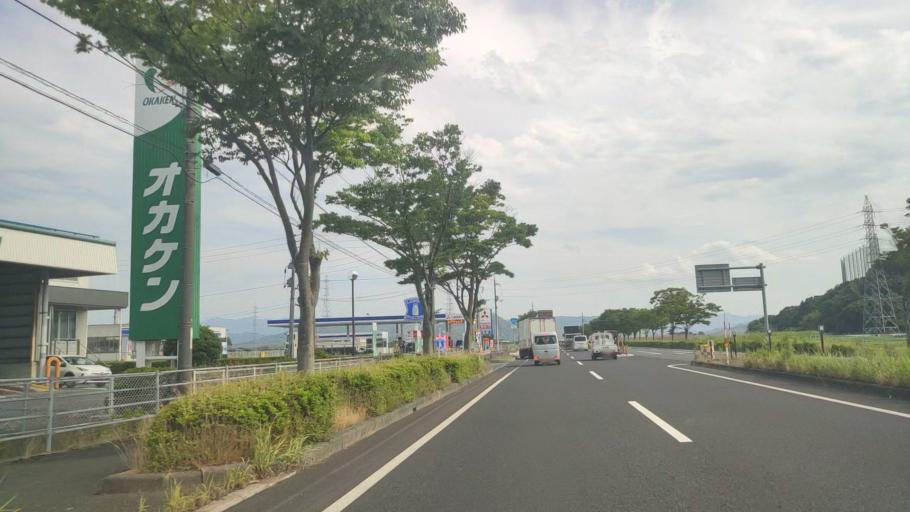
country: JP
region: Tottori
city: Tottori
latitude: 35.4893
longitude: 134.2043
